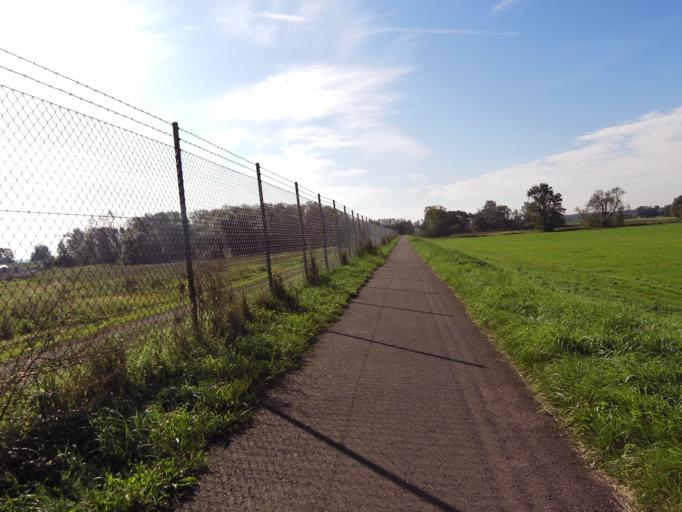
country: DE
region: Saxony-Anhalt
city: Coswig
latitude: 51.8739
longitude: 12.5184
